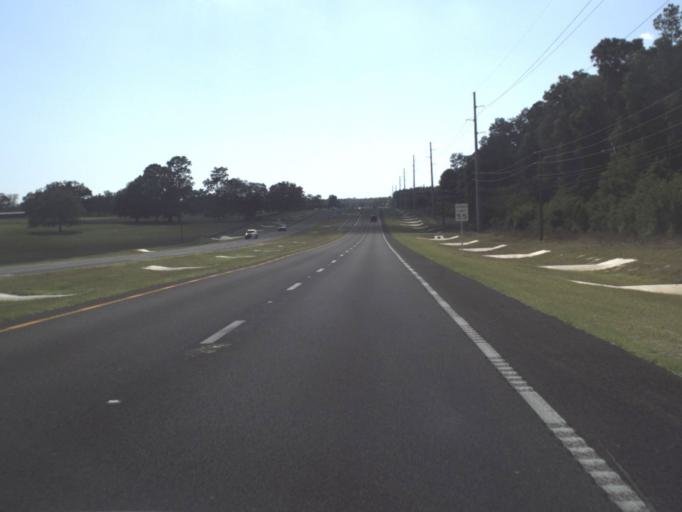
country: US
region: Florida
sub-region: Marion County
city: Ocala
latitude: 29.1869
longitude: -82.2854
